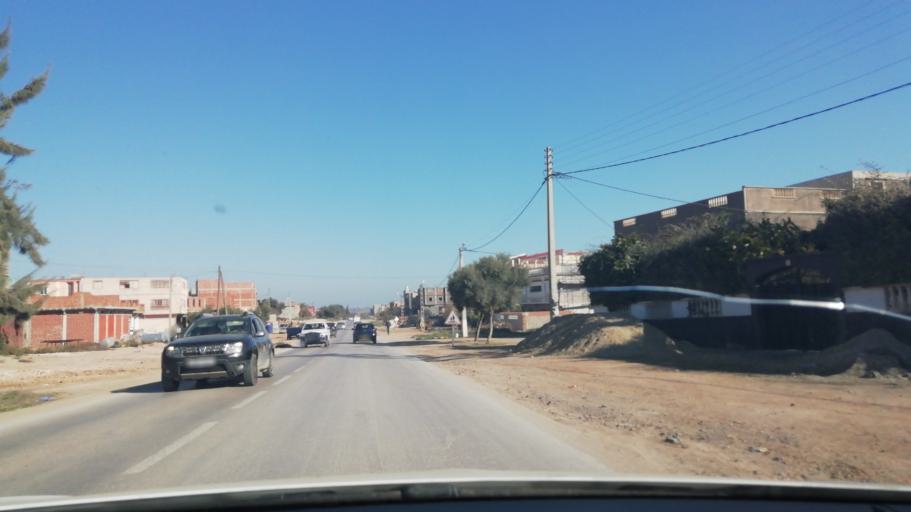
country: DZ
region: Tlemcen
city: Nedroma
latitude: 35.0134
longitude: -1.8986
